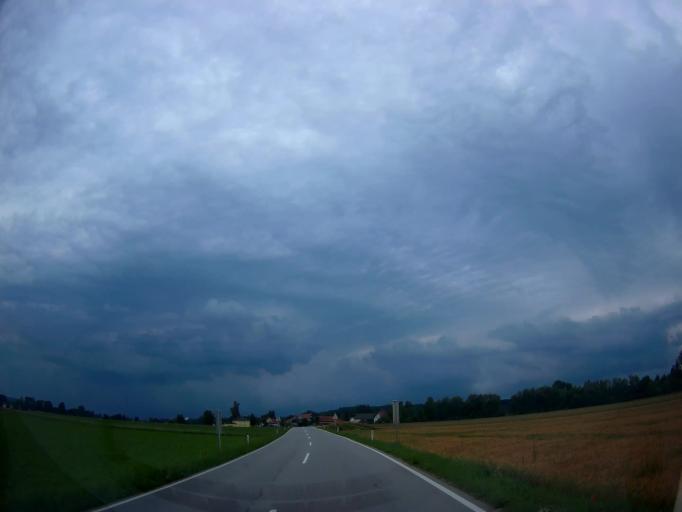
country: AT
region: Upper Austria
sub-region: Politischer Bezirk Braunau am Inn
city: Braunau am Inn
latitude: 48.1811
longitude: 13.1296
